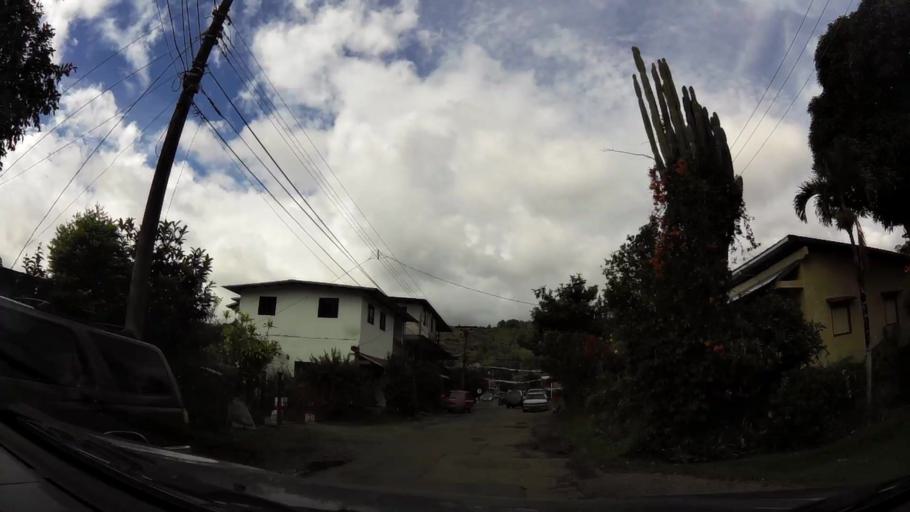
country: PA
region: Chiriqui
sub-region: Distrito Boquete
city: Boquete
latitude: 8.7752
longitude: -82.4309
